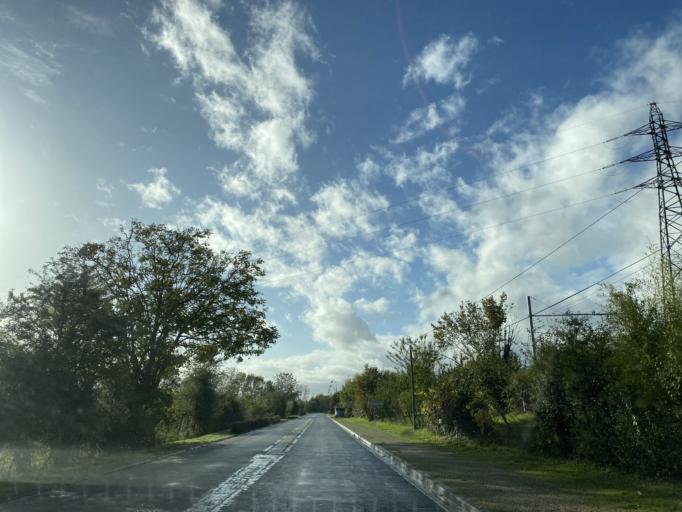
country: FR
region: Centre
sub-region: Departement du Cher
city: Saint-Doulchard
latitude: 47.0944
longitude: 2.3677
